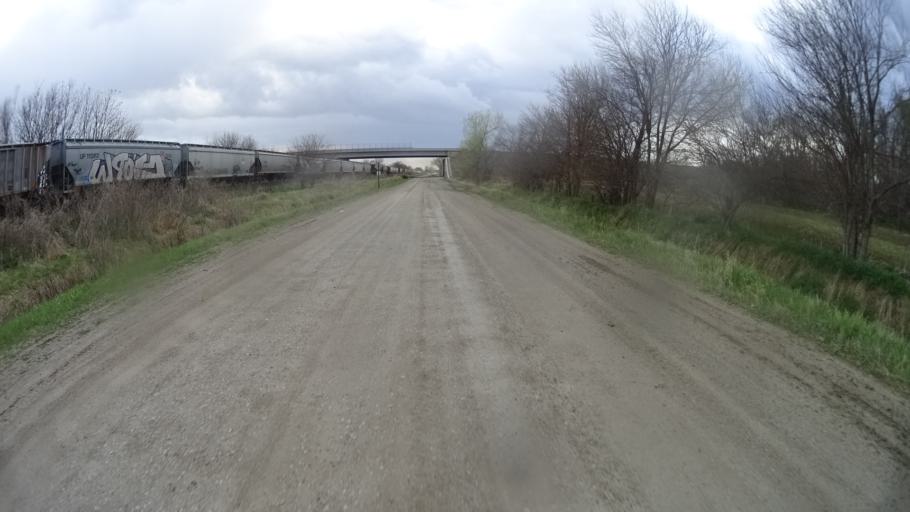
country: US
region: Nebraska
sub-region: Sarpy County
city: Offutt Air Force Base
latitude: 41.0830
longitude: -95.9175
